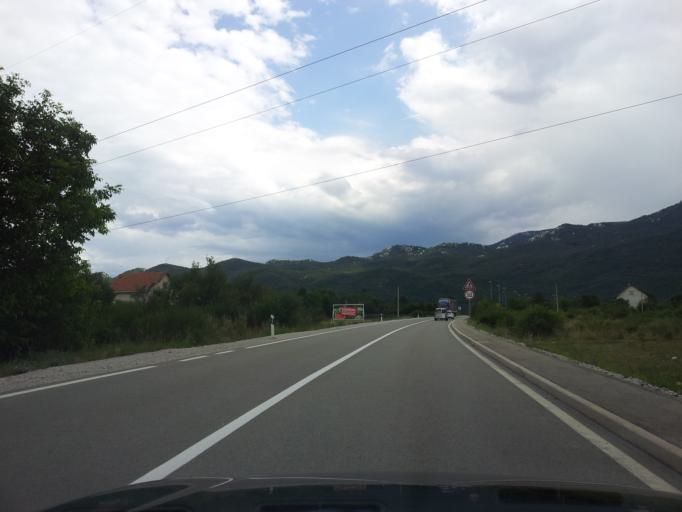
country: HR
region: Zadarska
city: Gracac
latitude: 44.3032
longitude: 15.8613
